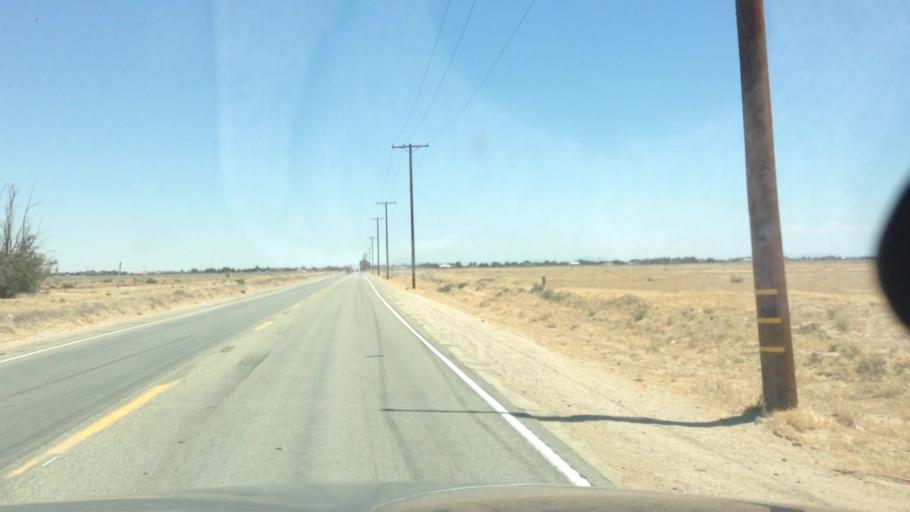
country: US
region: California
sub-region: Los Angeles County
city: Quartz Hill
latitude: 34.7764
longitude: -118.3079
